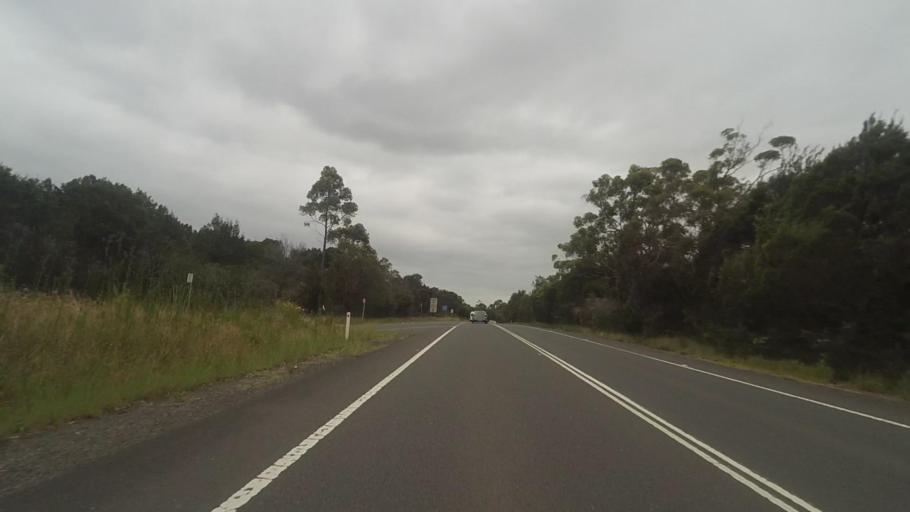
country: AU
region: New South Wales
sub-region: Sutherland Shire
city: Engadine
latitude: -34.0509
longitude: 150.9746
